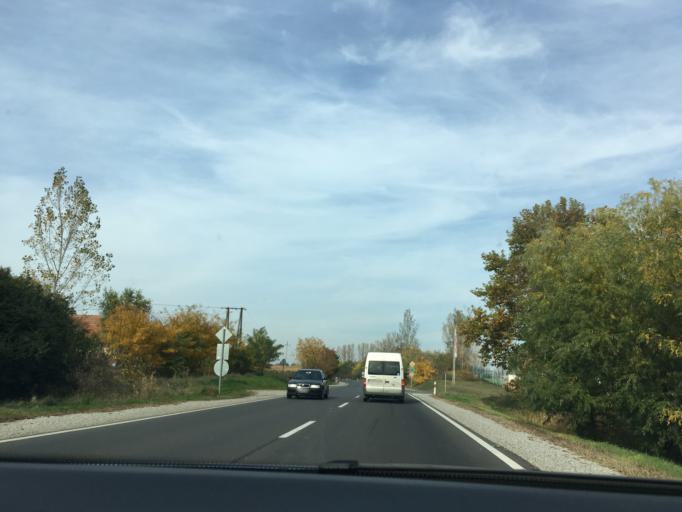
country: HU
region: Szabolcs-Szatmar-Bereg
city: Ujfeherto
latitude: 47.8043
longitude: 21.7042
